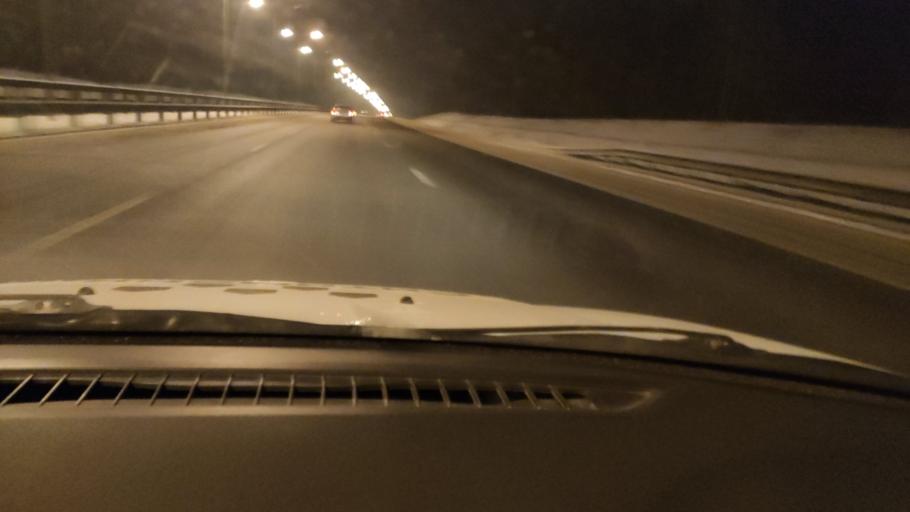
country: RU
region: Perm
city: Zvezdnyy
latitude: 57.7513
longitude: 56.3335
